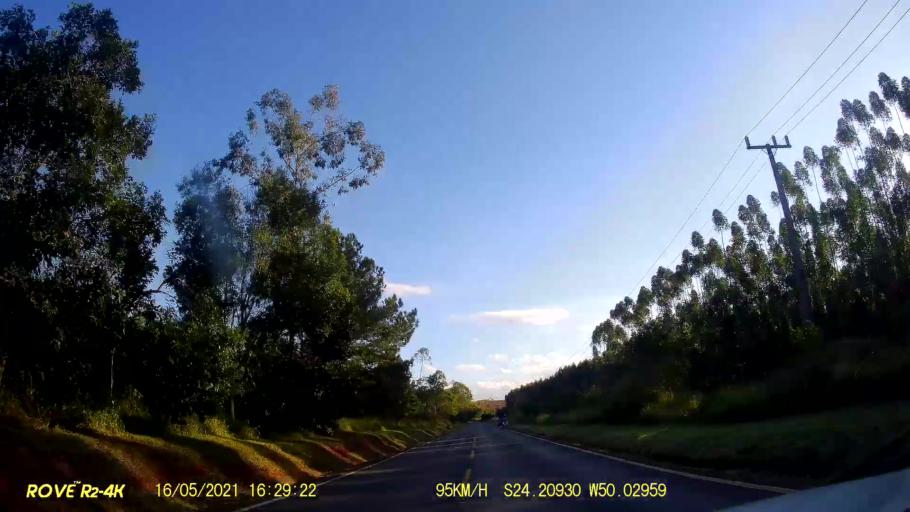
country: BR
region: Parana
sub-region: Jaguariaiva
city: Jaguariaiva
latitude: -24.2094
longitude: -50.0297
